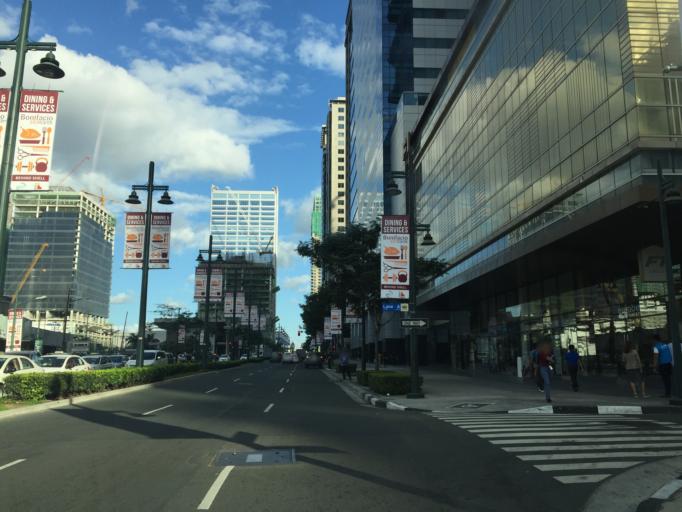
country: PH
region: Metro Manila
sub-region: Makati City
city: Makati City
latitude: 14.5539
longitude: 121.0491
